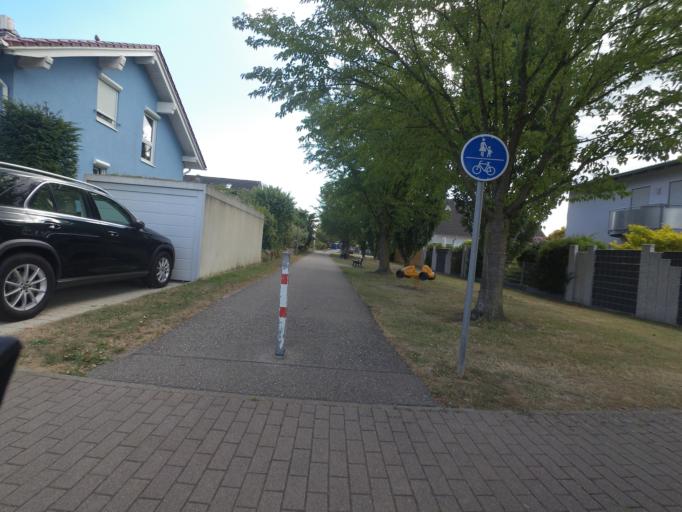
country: DE
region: Baden-Wuerttemberg
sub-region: Karlsruhe Region
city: Sinzheim
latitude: 48.7746
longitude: 8.1660
